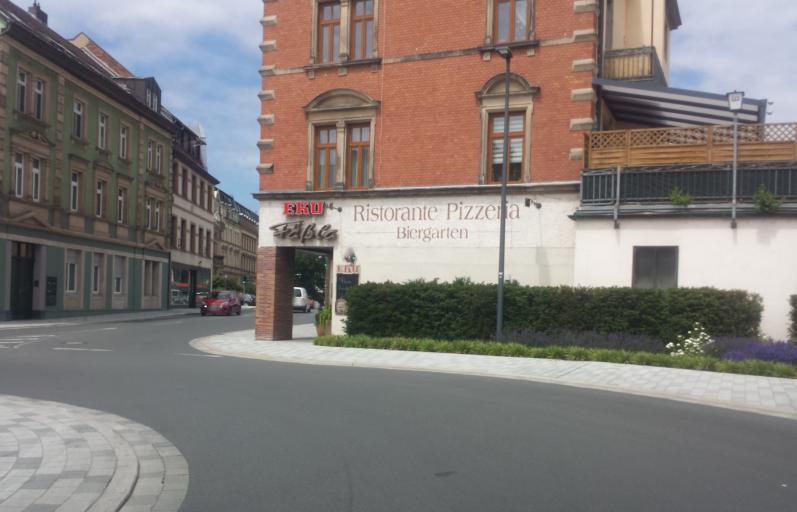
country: DE
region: Bavaria
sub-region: Upper Franconia
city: Kulmbach
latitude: 50.1091
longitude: 11.4569
